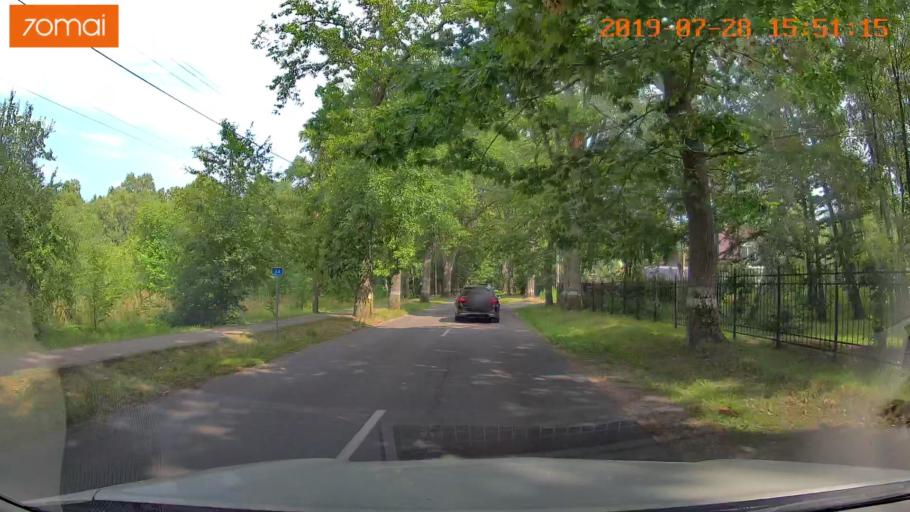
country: RU
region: Kaliningrad
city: Otradnoye
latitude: 54.9415
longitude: 20.1027
